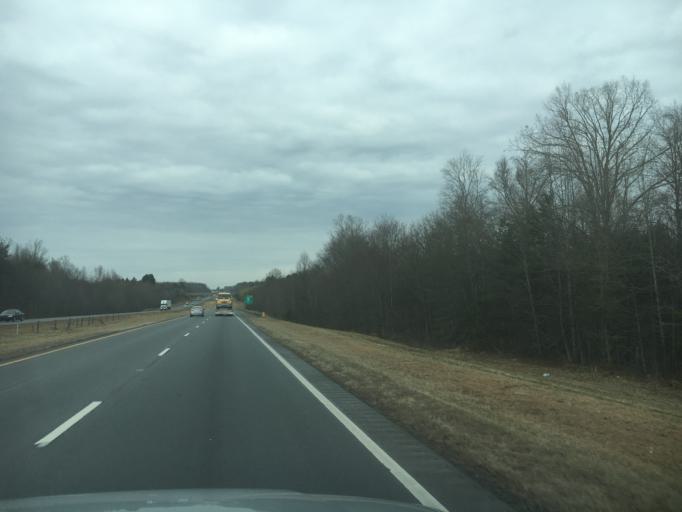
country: US
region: North Carolina
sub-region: Lincoln County
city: Lincolnton
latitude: 35.5086
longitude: -81.2237
